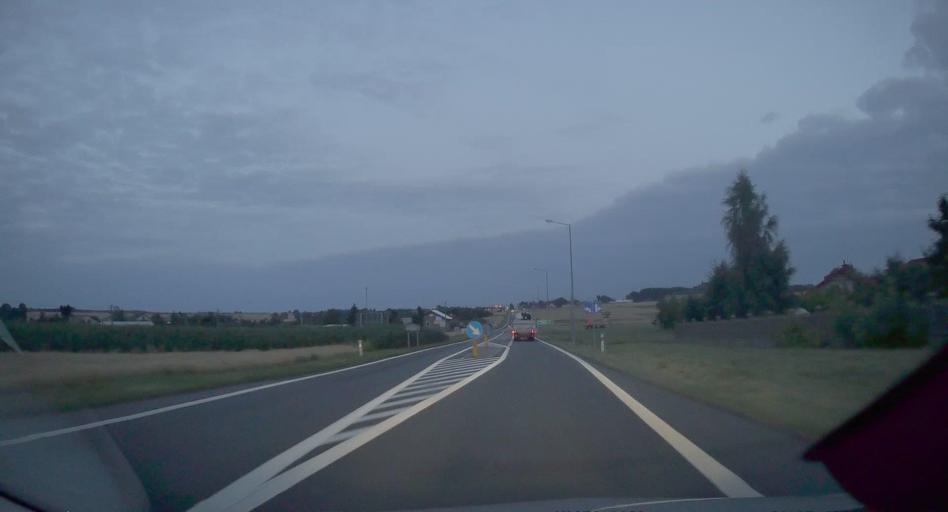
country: PL
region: Silesian Voivodeship
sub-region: Powiat klobucki
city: Opatow
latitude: 50.9352
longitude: 18.8505
